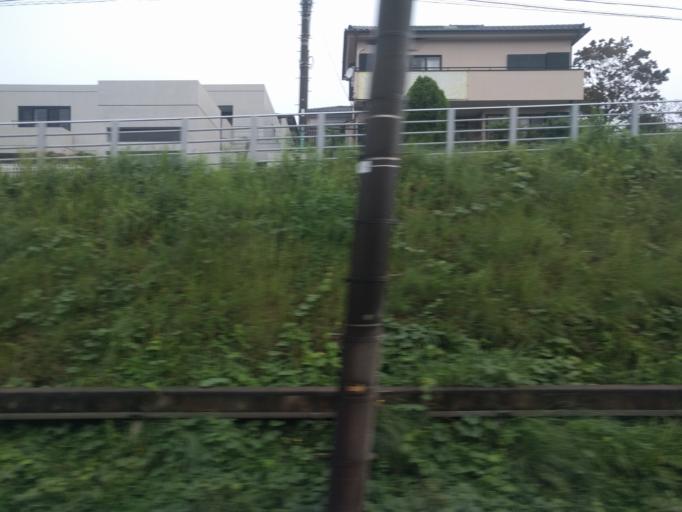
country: JP
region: Kanagawa
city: Minami-rinkan
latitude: 35.5114
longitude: 139.4679
